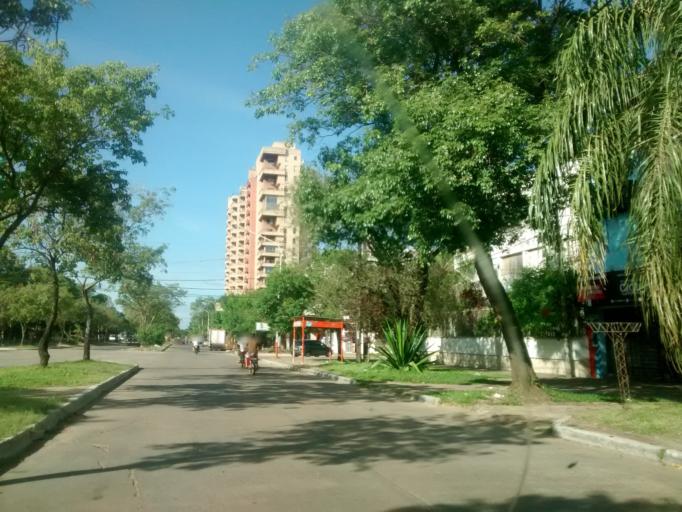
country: AR
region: Chaco
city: Resistencia
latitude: -27.4618
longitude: -58.9843
